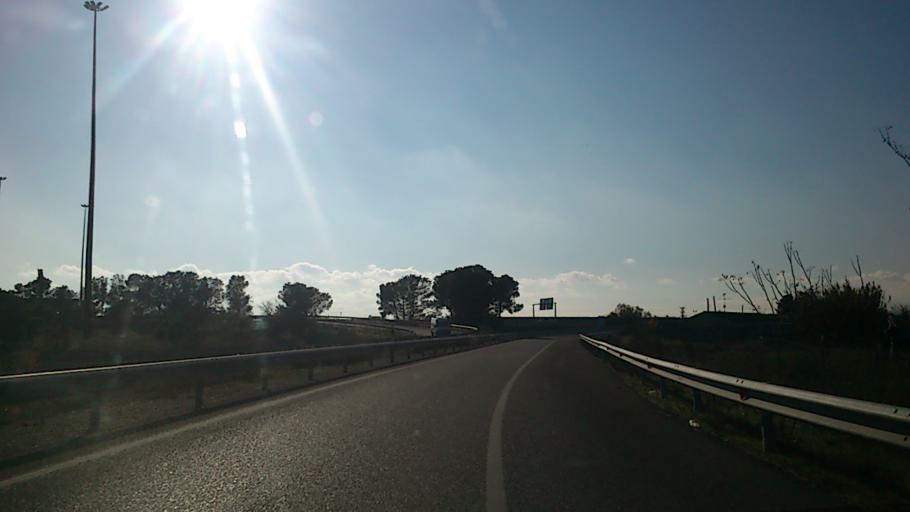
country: ES
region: Aragon
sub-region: Provincia de Zaragoza
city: Zaragoza
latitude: 41.6776
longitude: -0.8352
